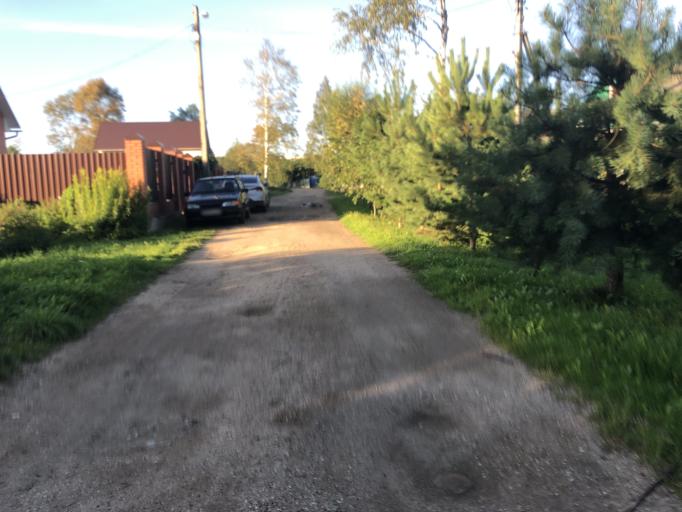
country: RU
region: Tverskaya
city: Rzhev
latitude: 56.2438
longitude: 34.3076
